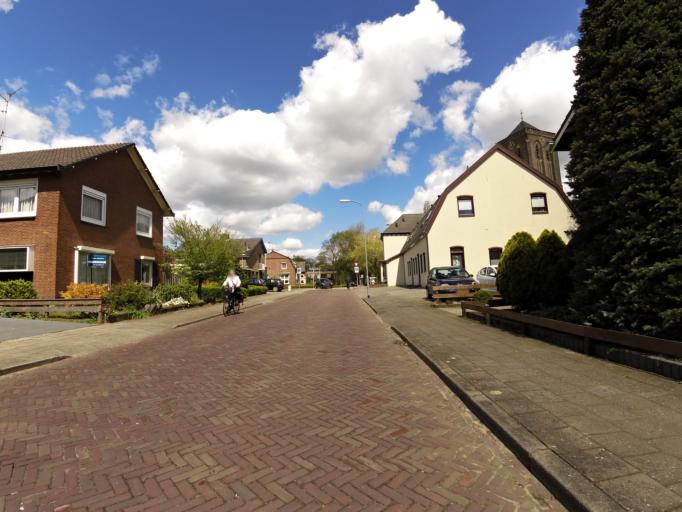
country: NL
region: Gelderland
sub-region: Gemeente Zevenaar
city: Zevenaar
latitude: 51.9372
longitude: 6.1257
